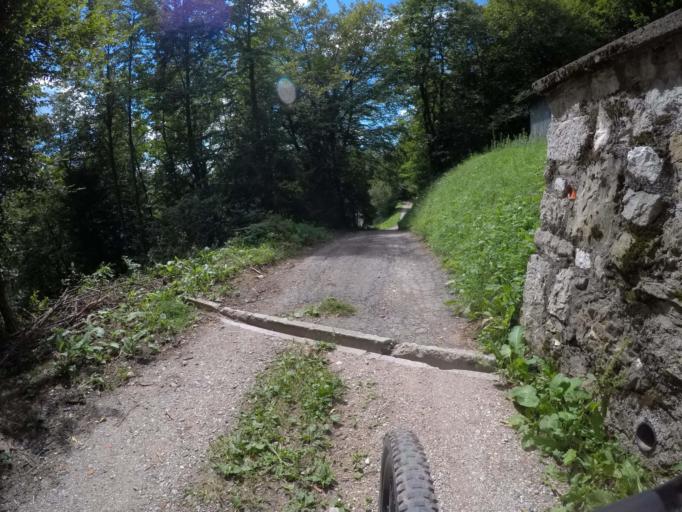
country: IT
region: Friuli Venezia Giulia
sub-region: Provincia di Udine
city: Zuglio
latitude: 46.4757
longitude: 13.0588
